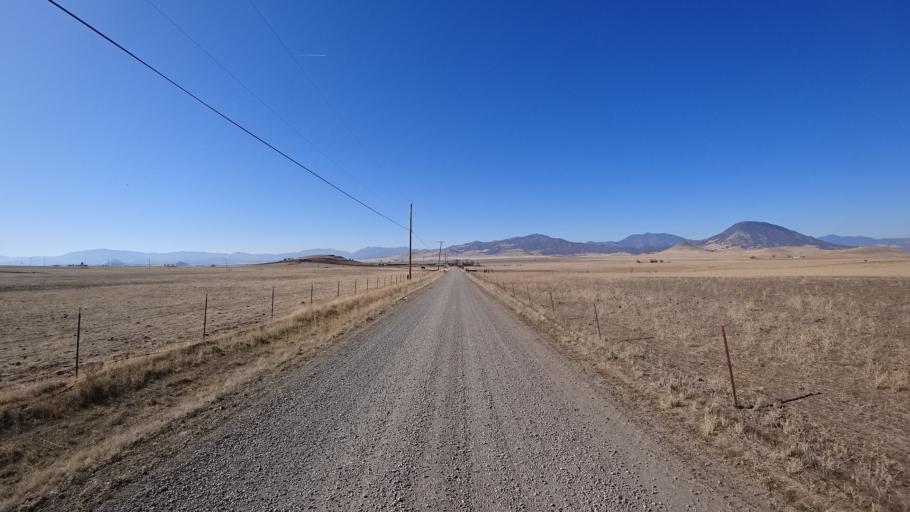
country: US
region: California
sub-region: Siskiyou County
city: Montague
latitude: 41.7939
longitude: -122.4213
